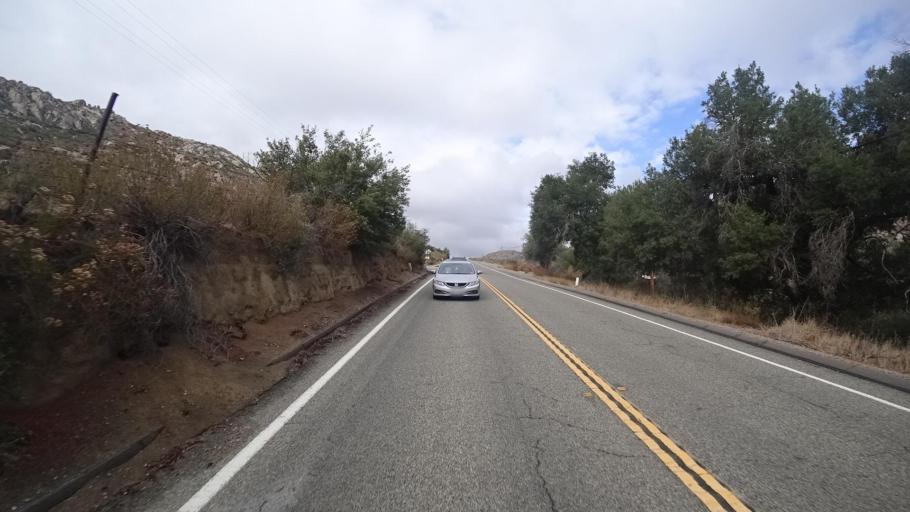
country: MX
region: Baja California
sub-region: Tecate
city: Hacienda Tecate
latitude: 32.5960
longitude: -116.5452
